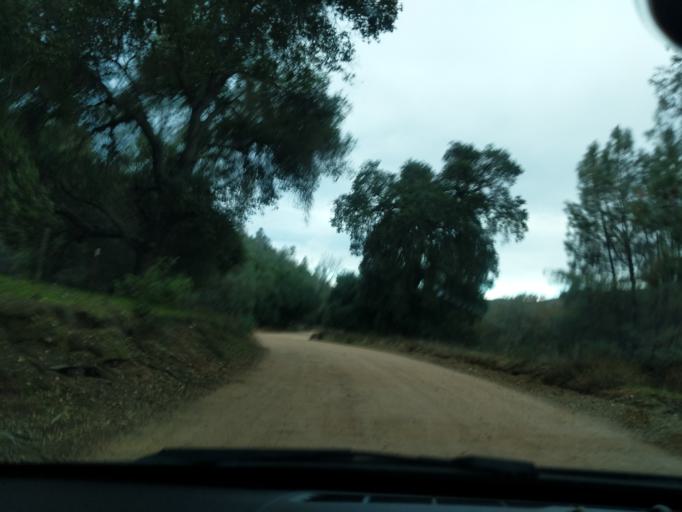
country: US
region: California
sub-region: Monterey County
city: Soledad
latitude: 36.5652
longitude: -121.2180
